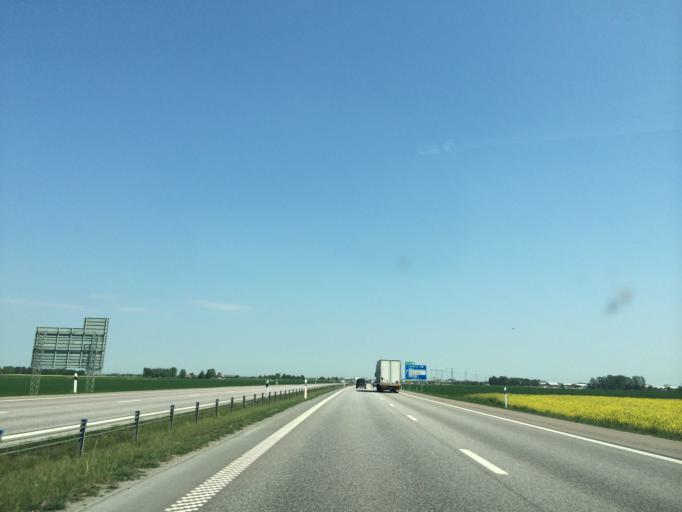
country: SE
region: OEstergoetland
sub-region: Linkopings Kommun
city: Malmslatt
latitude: 58.4386
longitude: 15.5569
